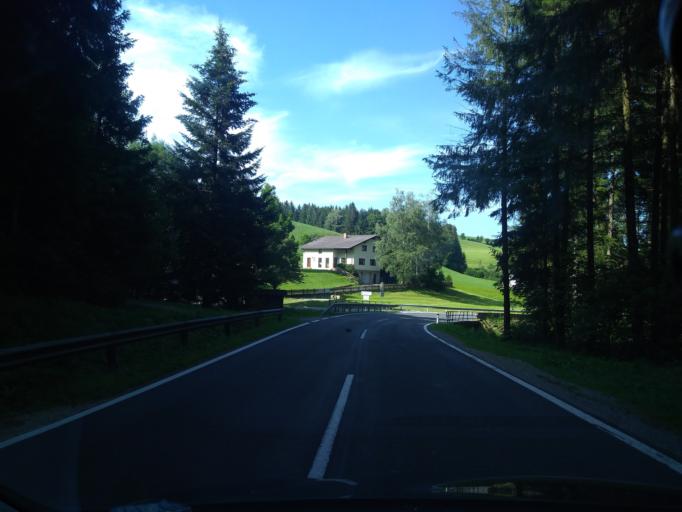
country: AT
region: Styria
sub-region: Politischer Bezirk Weiz
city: Passail
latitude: 47.2704
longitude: 15.4531
